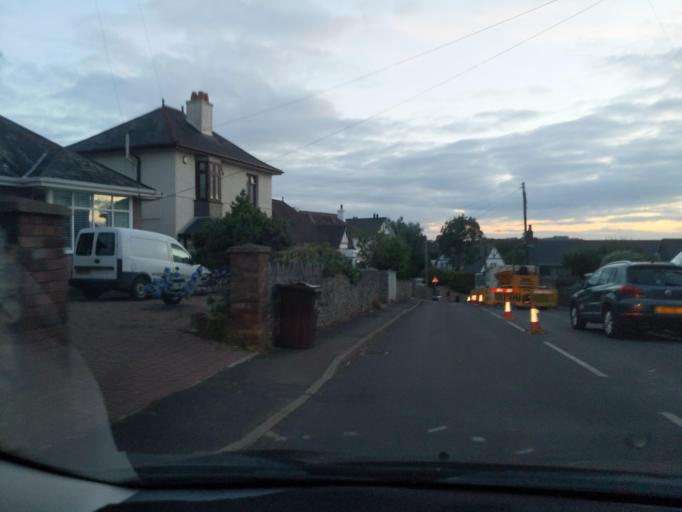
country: GB
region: England
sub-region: Plymouth
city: Plymstock
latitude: 50.3605
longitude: -4.1034
